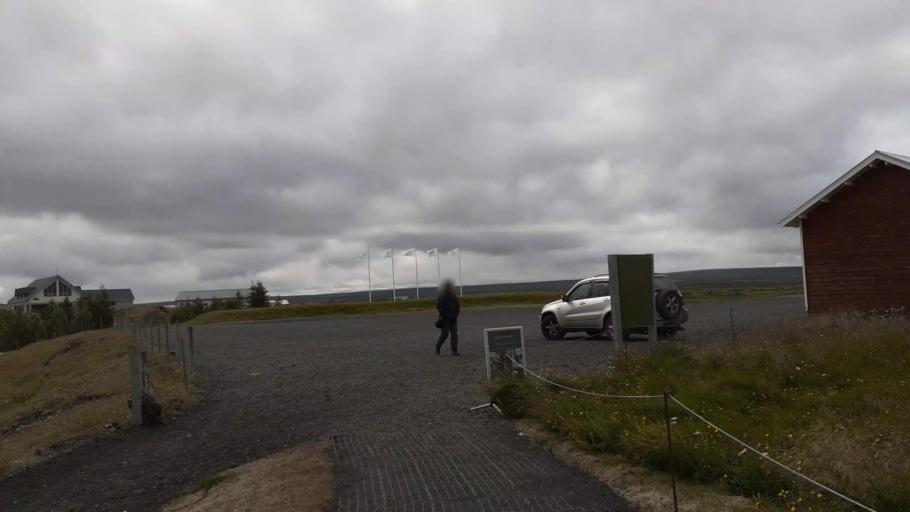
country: IS
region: Northeast
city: Laugar
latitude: 65.5687
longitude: -17.0377
